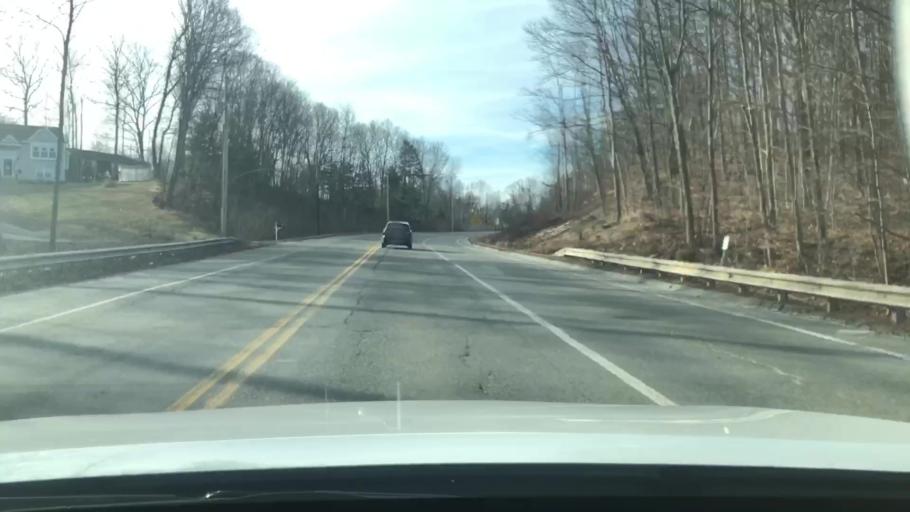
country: US
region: Massachusetts
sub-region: Worcester County
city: Grafton
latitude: 42.2049
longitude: -71.6691
